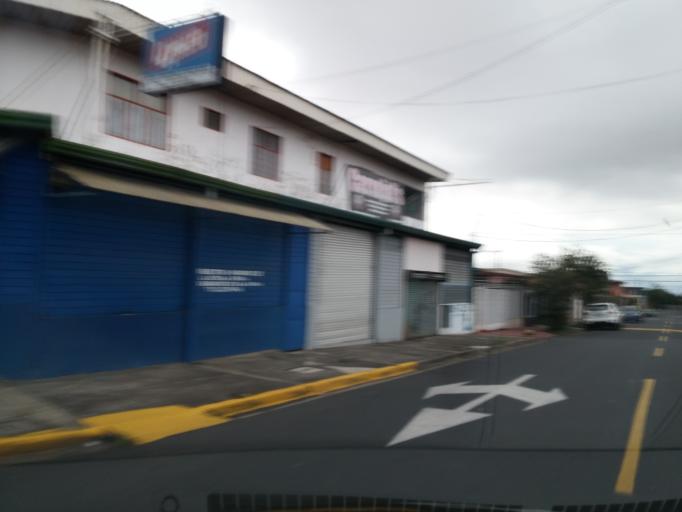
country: CR
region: Heredia
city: San Francisco
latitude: 9.9998
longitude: -84.1258
